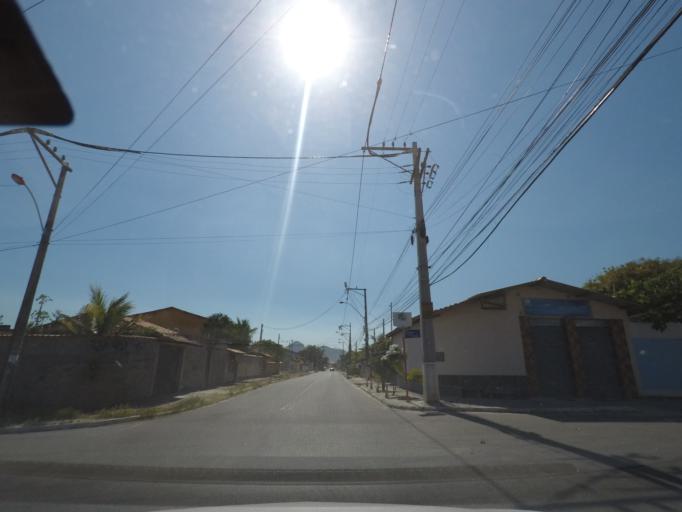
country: BR
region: Rio de Janeiro
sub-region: Marica
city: Marica
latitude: -22.9671
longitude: -42.9576
